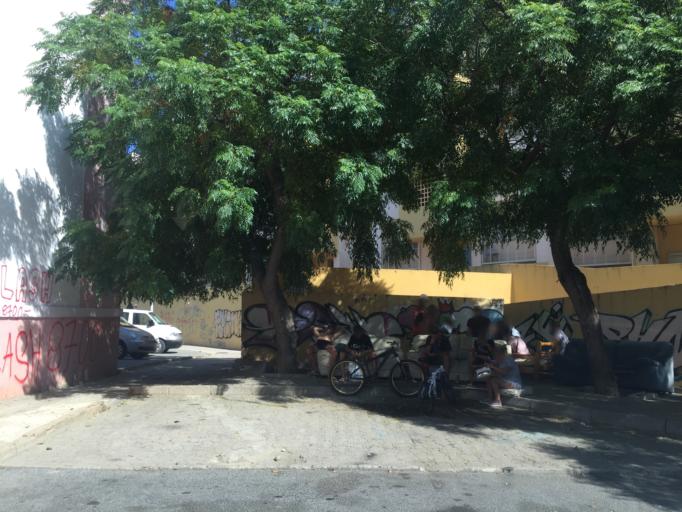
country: PT
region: Faro
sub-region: Olhao
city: Olhao
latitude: 37.0328
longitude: -7.8331
